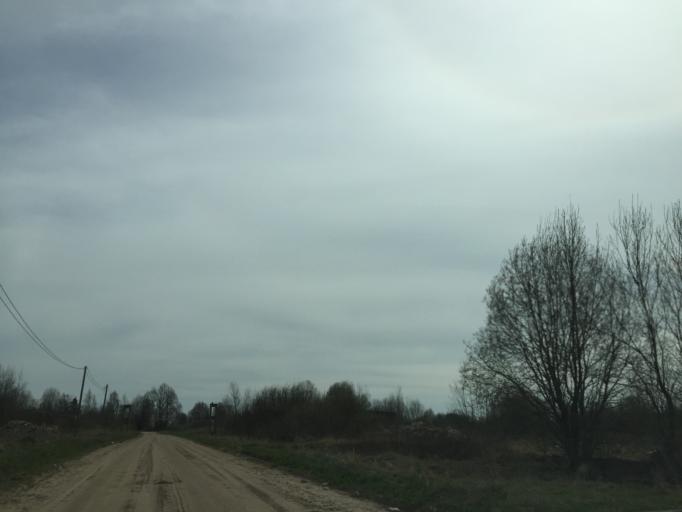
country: LV
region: Ludzas Rajons
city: Ludza
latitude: 56.5149
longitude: 27.5417
